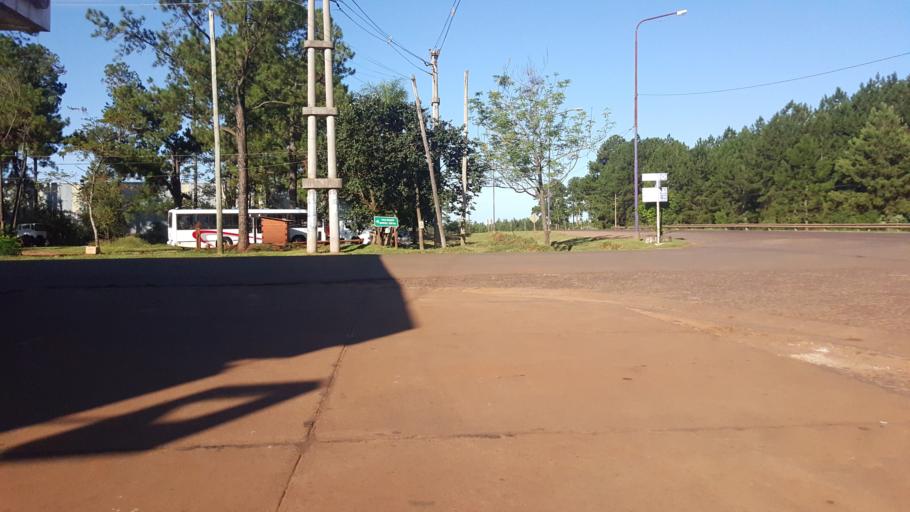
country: AR
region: Misiones
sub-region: Departamento de San Ignacio
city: San Ignacio
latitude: -27.2675
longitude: -55.5393
